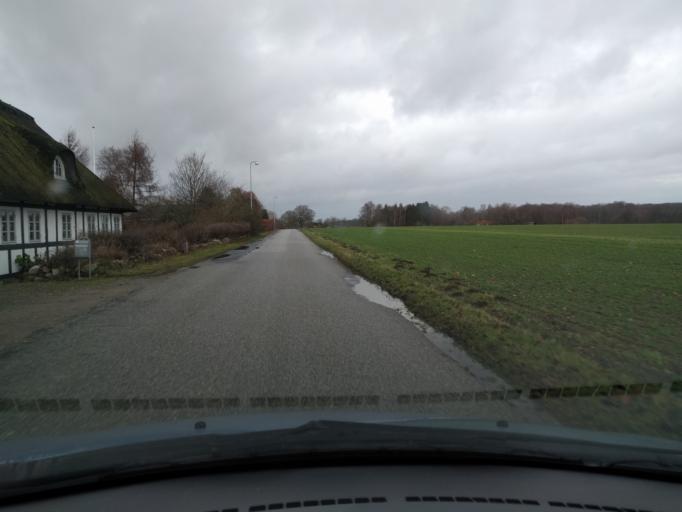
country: DK
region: South Denmark
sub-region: Kerteminde Kommune
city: Langeskov
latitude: 55.3456
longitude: 10.5452
